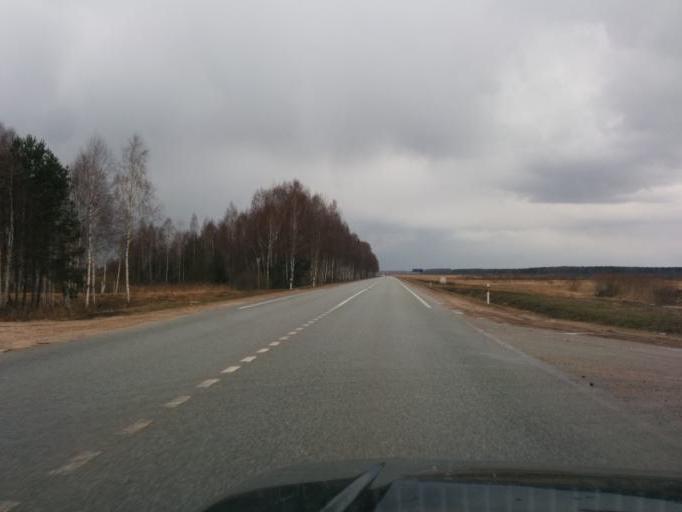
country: LV
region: Marupe
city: Marupe
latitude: 56.8488
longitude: 24.0104
